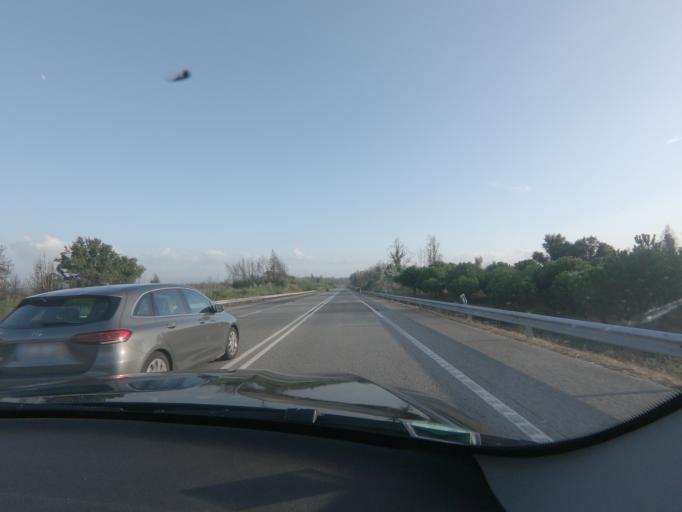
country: PT
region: Viseu
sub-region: Concelho de Tondela
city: Tondela
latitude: 40.4632
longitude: -8.1011
